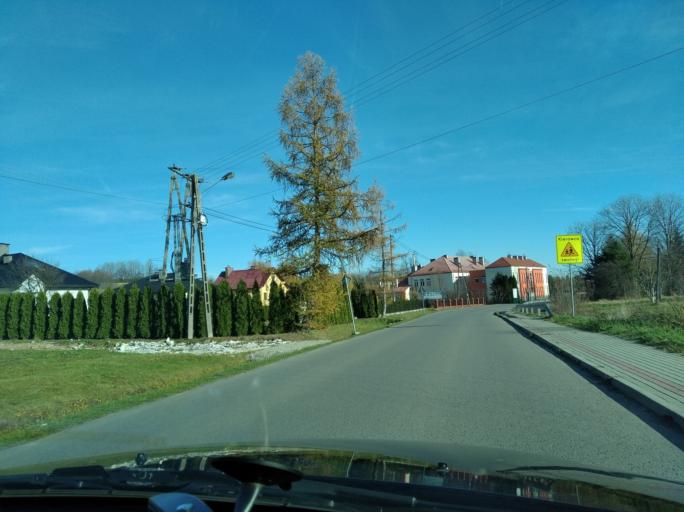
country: PL
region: Subcarpathian Voivodeship
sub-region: Powiat rzeszowski
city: Niechobrz
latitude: 49.9783
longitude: 21.8901
